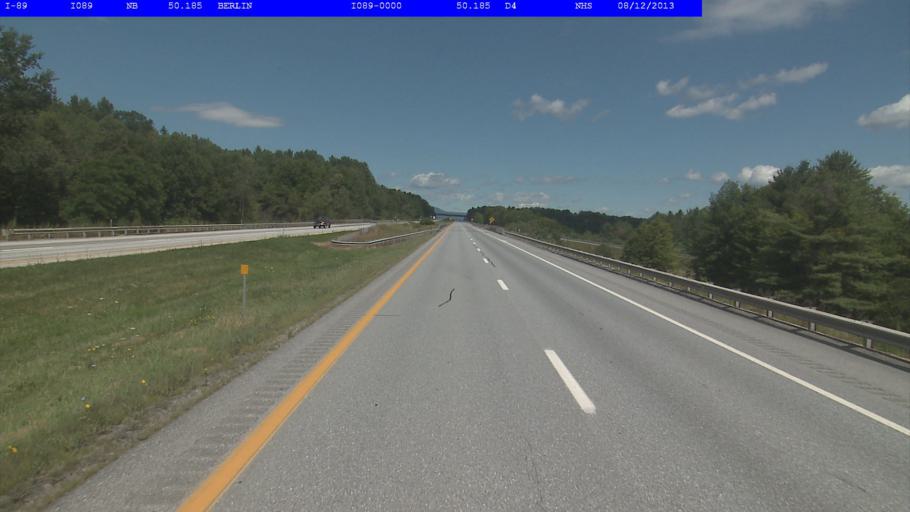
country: US
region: Vermont
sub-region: Washington County
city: Montpelier
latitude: 44.2143
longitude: -72.5833
